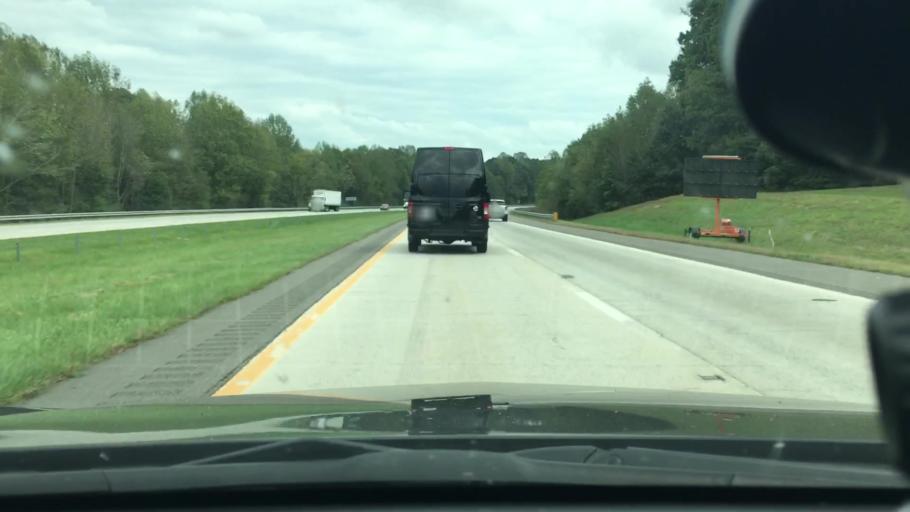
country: US
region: North Carolina
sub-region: Davie County
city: Mocksville
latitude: 35.8660
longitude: -80.7333
